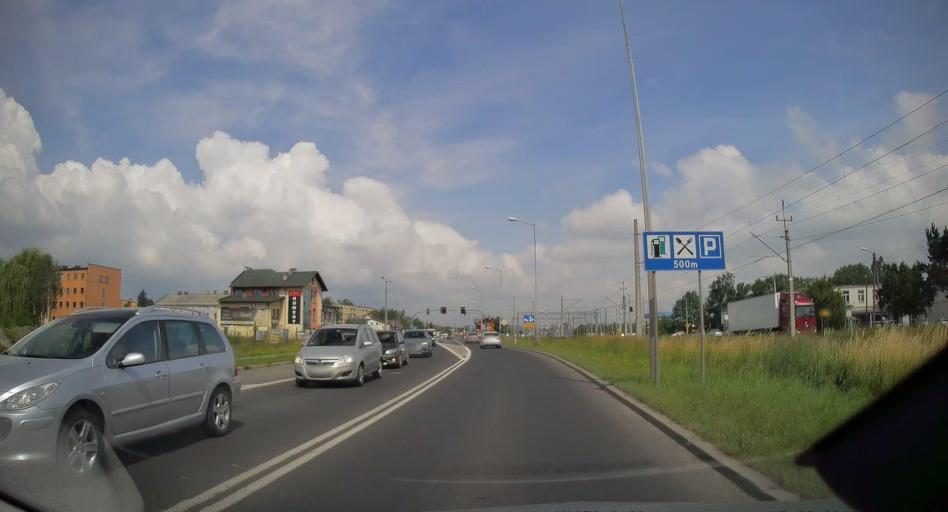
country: PL
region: Lesser Poland Voivodeship
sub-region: Powiat wadowicki
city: Wadowice
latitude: 49.8823
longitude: 19.5043
